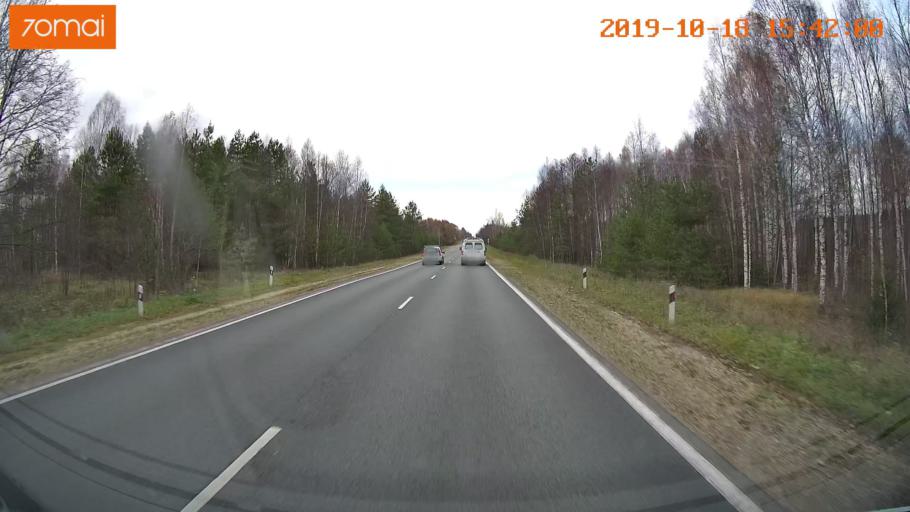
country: RU
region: Vladimir
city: Golovino
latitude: 55.9512
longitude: 40.5744
